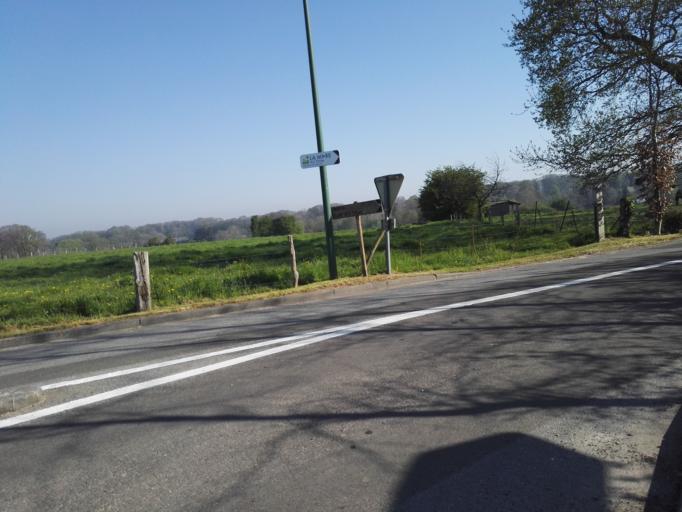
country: FR
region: Haute-Normandie
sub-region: Departement de la Seine-Maritime
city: Grainville-la-Teinturiere
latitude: 49.7385
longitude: 0.7103
